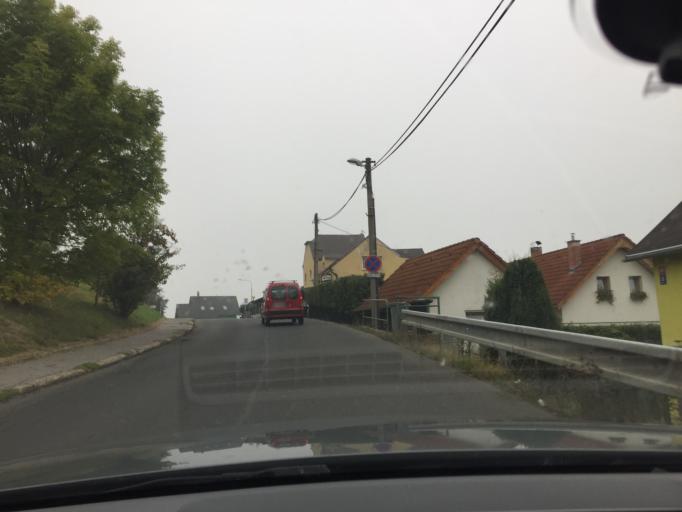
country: CZ
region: Ustecky
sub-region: Okres Usti nad Labem
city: Usti nad Labem
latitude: 50.6852
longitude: 14.0404
